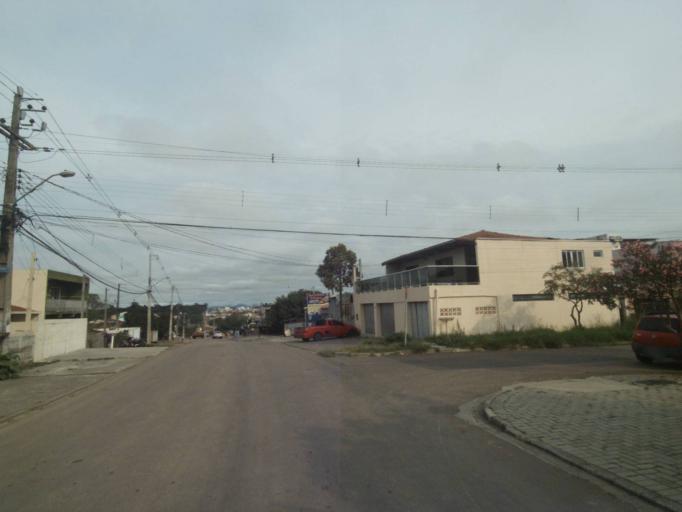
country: BR
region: Parana
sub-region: Sao Jose Dos Pinhais
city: Sao Jose dos Pinhais
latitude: -25.5523
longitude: -49.2696
